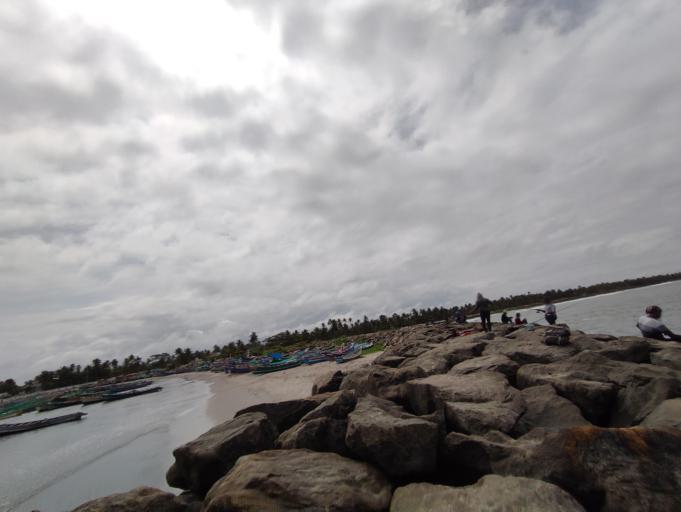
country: IN
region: Kerala
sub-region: Alappuzha
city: Kutiatodu
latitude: 9.7985
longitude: 76.2735
